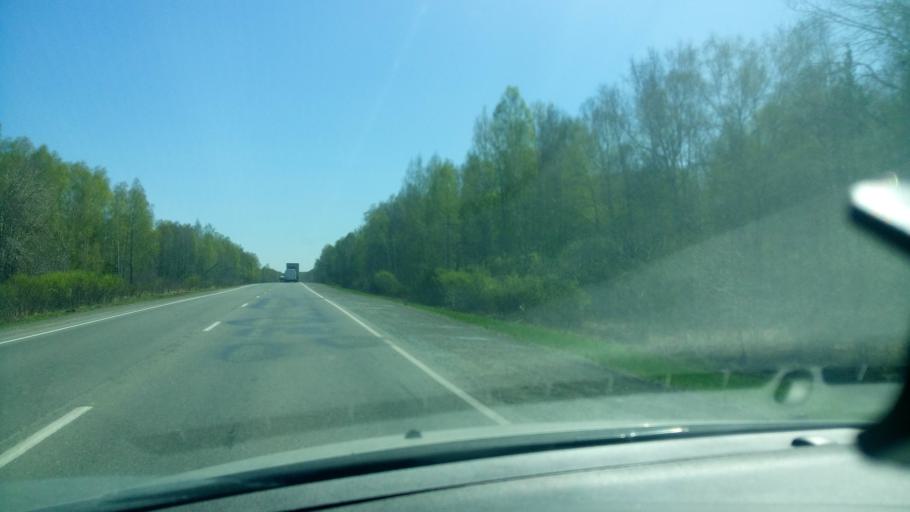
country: RU
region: Sverdlovsk
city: Bogdanovich
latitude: 56.7543
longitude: 62.1784
